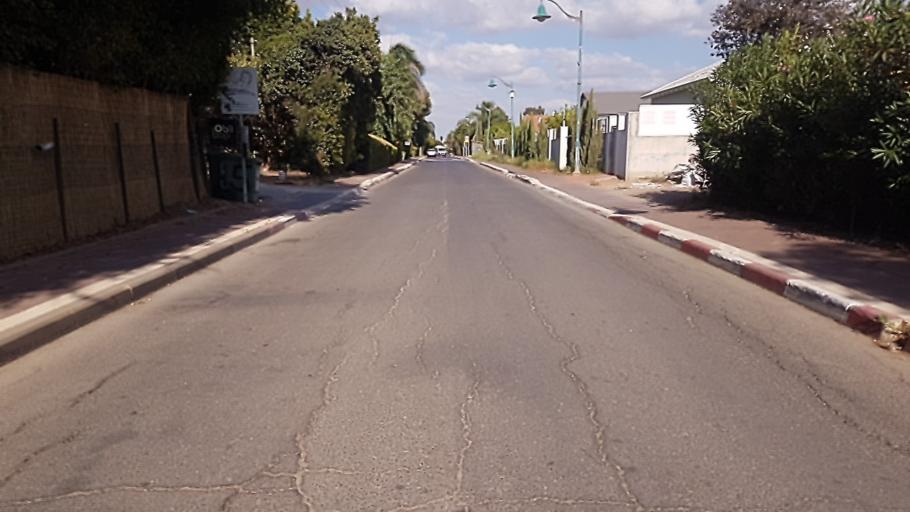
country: IL
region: Central District
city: Jaljulya
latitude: 32.1722
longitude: 34.9341
